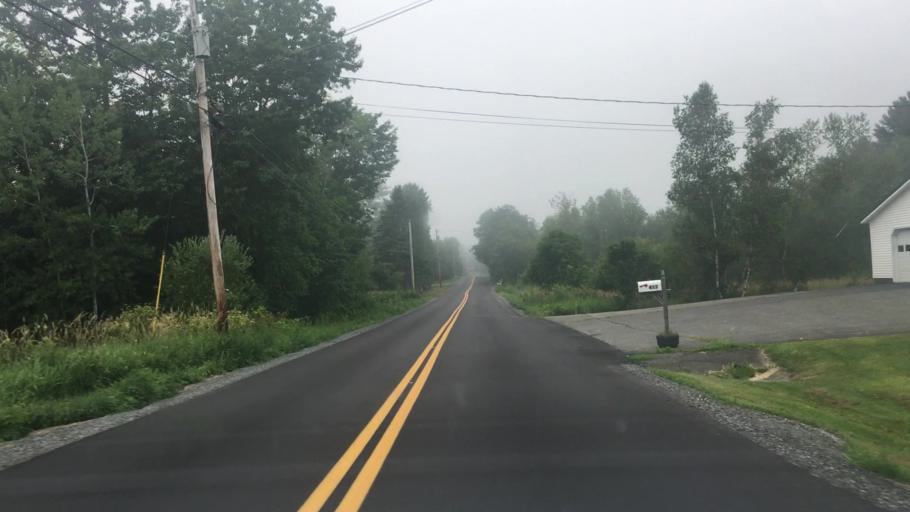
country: US
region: Maine
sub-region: Kennebec County
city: Oakland
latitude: 44.5170
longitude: -69.7206
